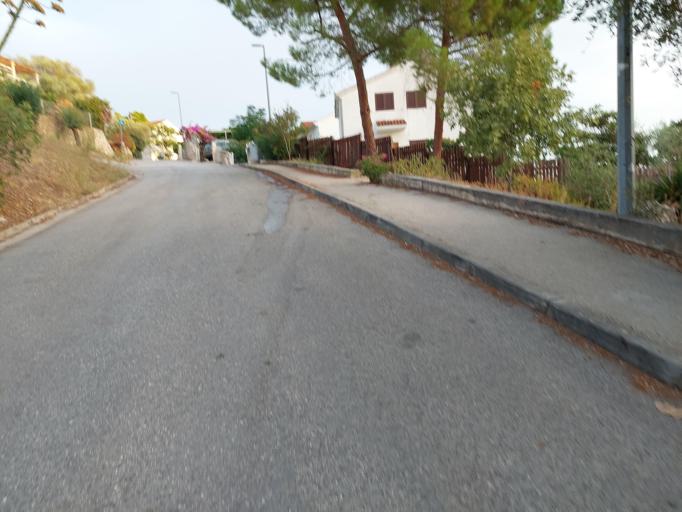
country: HR
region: Splitsko-Dalmatinska
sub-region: Grad Trogir
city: Trogir
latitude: 43.4934
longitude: 16.2734
